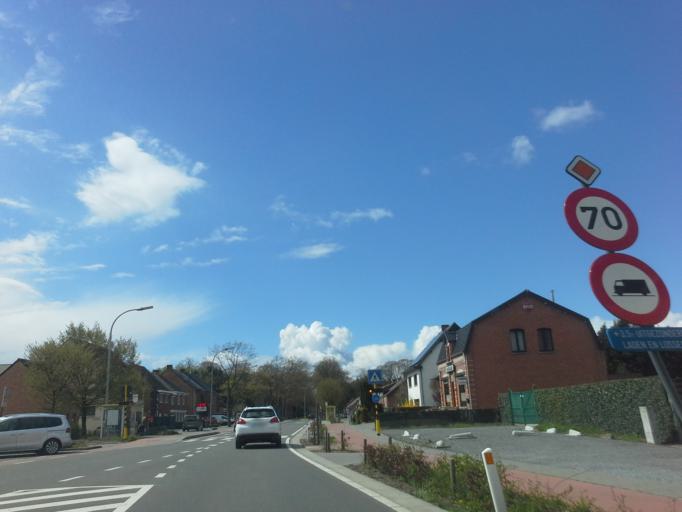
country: BE
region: Flanders
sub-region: Provincie Antwerpen
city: Balen
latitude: 51.2243
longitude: 5.2276
